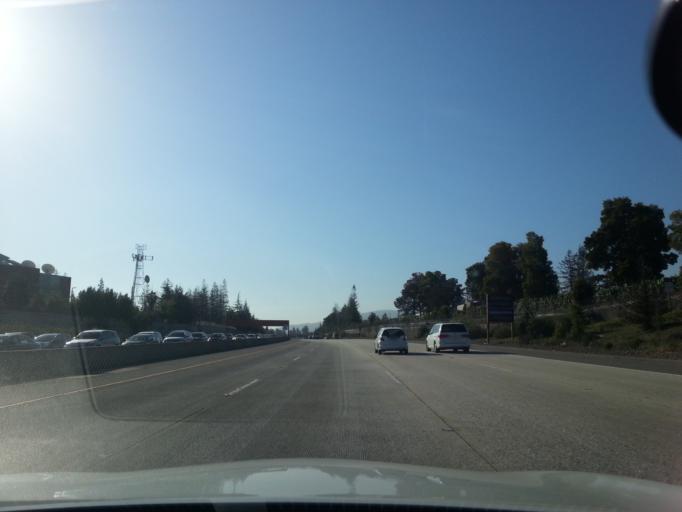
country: US
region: California
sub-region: Santa Clara County
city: Cupertino
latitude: 37.3219
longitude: -122.0498
